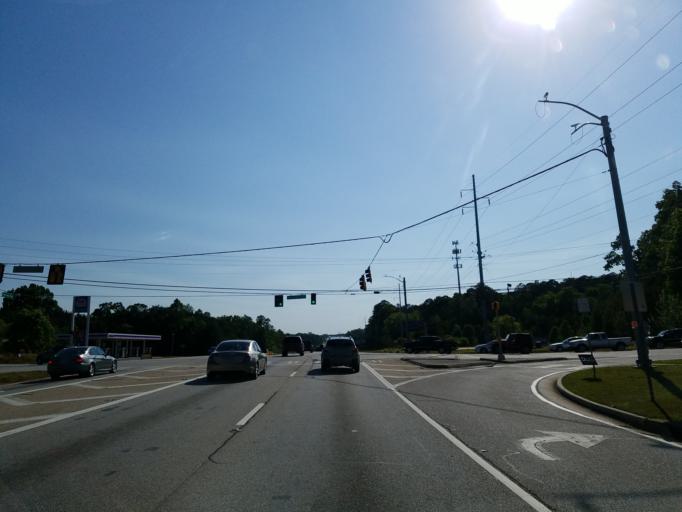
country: US
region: Georgia
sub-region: Paulding County
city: Hiram
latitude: 33.9264
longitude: -84.7475
